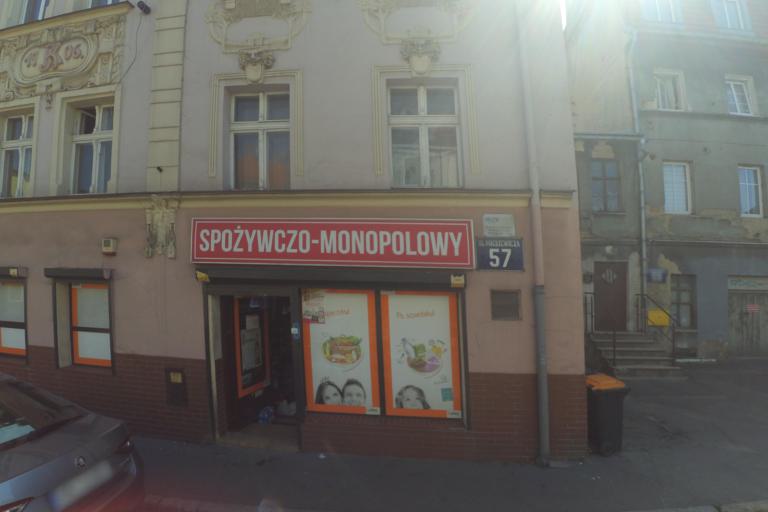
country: PL
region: Lower Silesian Voivodeship
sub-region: Powiat walbrzyski
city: Walbrzych
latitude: 50.7610
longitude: 16.2842
